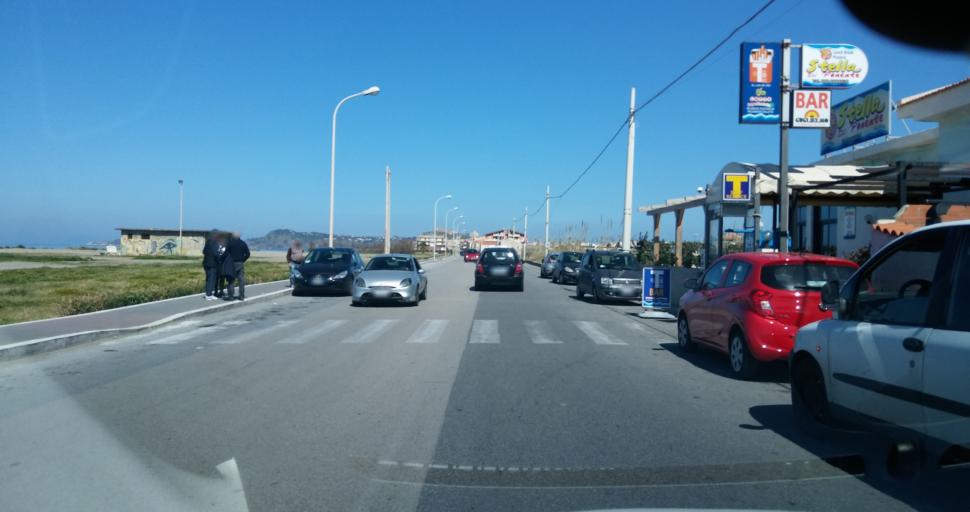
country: IT
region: Sicily
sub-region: Messina
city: Milazzo
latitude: 38.2025
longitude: 15.2255
